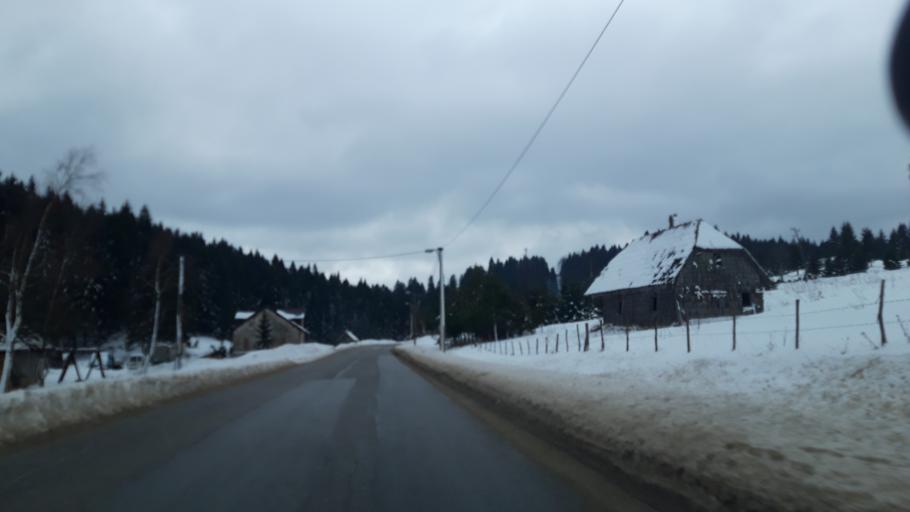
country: BA
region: Republika Srpska
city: Han Pijesak
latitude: 44.0920
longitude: 18.9549
